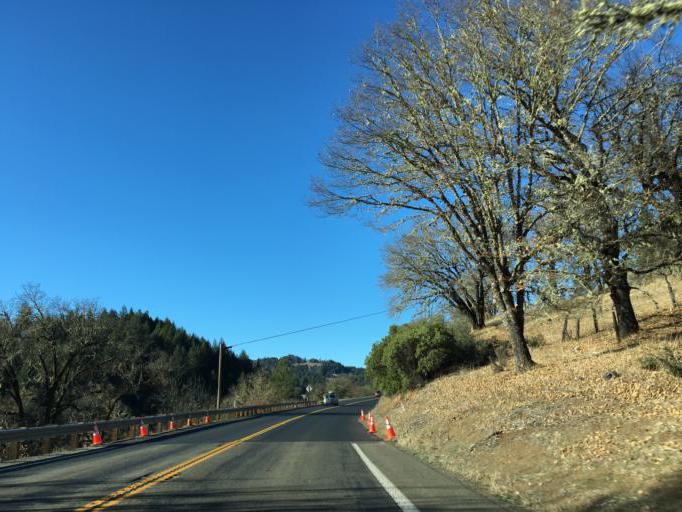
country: US
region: California
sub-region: Mendocino County
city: Laytonville
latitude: 39.7501
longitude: -123.5335
